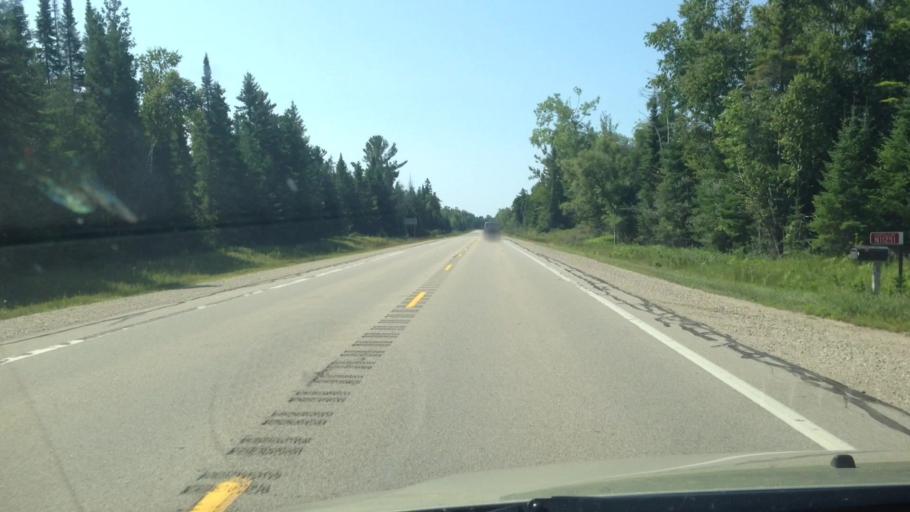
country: US
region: Michigan
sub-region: Delta County
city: Escanaba
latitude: 45.5188
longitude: -87.2886
